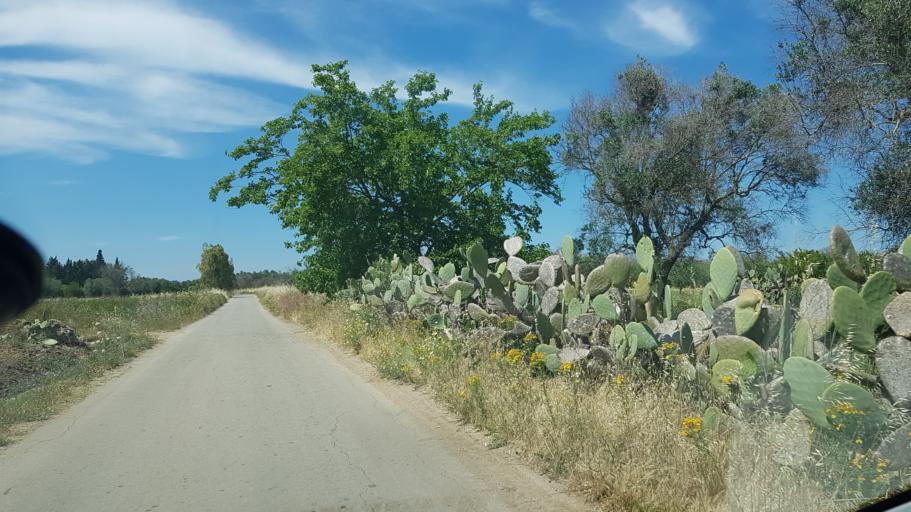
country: IT
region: Apulia
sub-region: Provincia di Brindisi
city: San Pietro Vernotico
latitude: 40.5218
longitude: 18.0116
